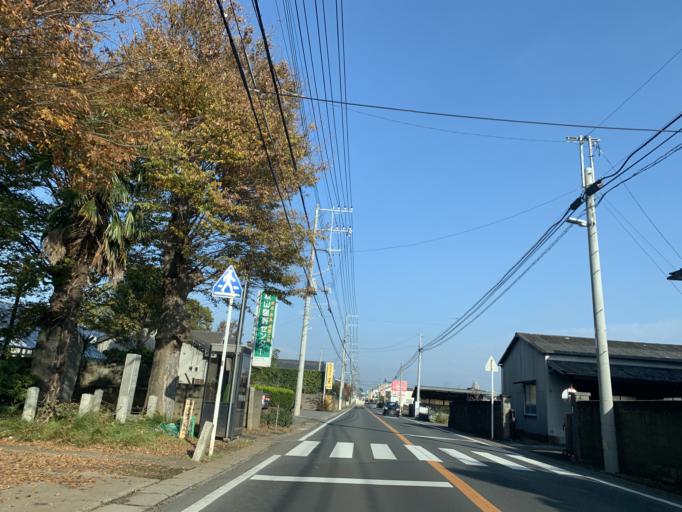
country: JP
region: Chiba
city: Nagareyama
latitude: 35.8651
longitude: 139.9288
